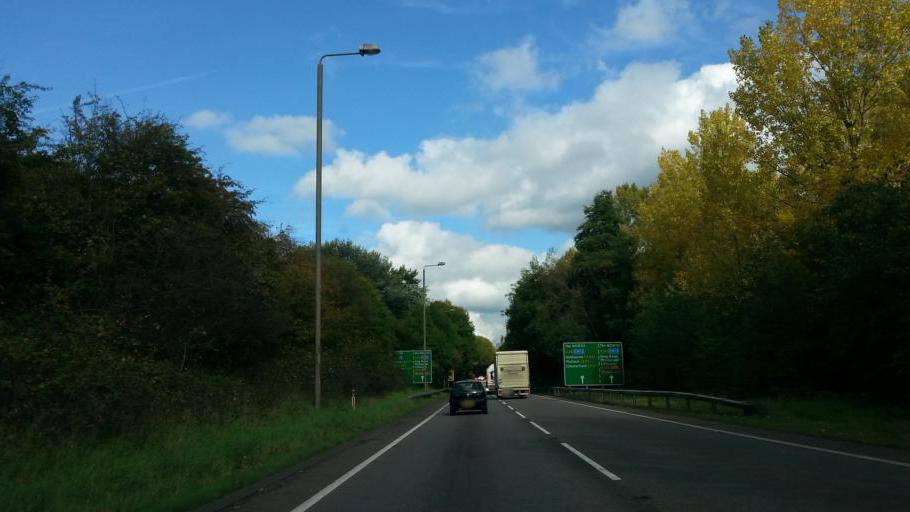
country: GB
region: England
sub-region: Derby
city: Derby
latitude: 52.9182
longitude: -1.5189
